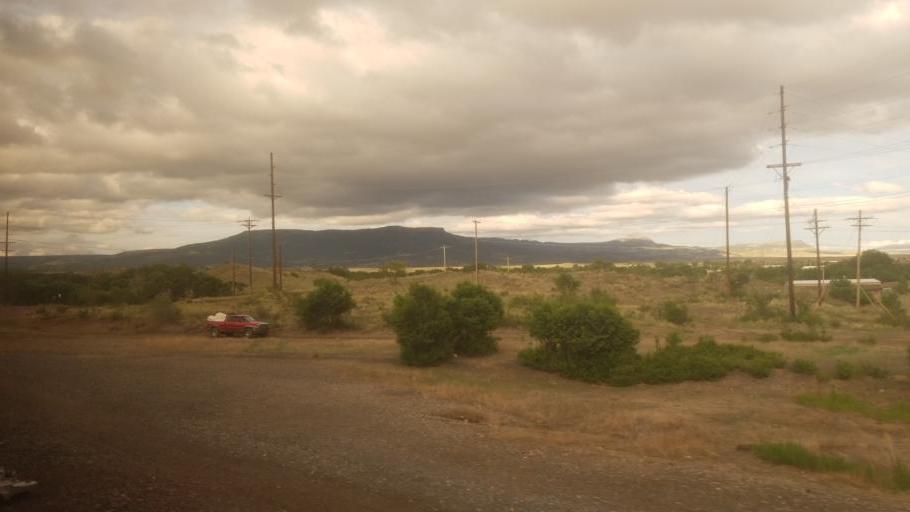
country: US
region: New Mexico
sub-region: Colfax County
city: Raton
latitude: 36.8920
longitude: -104.4403
